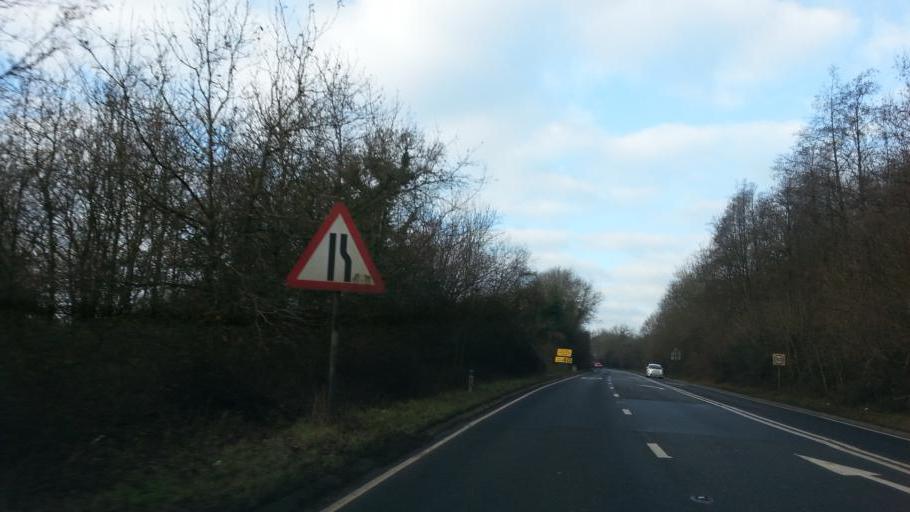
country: GB
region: England
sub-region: South Gloucestershire
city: Cold Ashton
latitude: 51.4215
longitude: -2.3540
